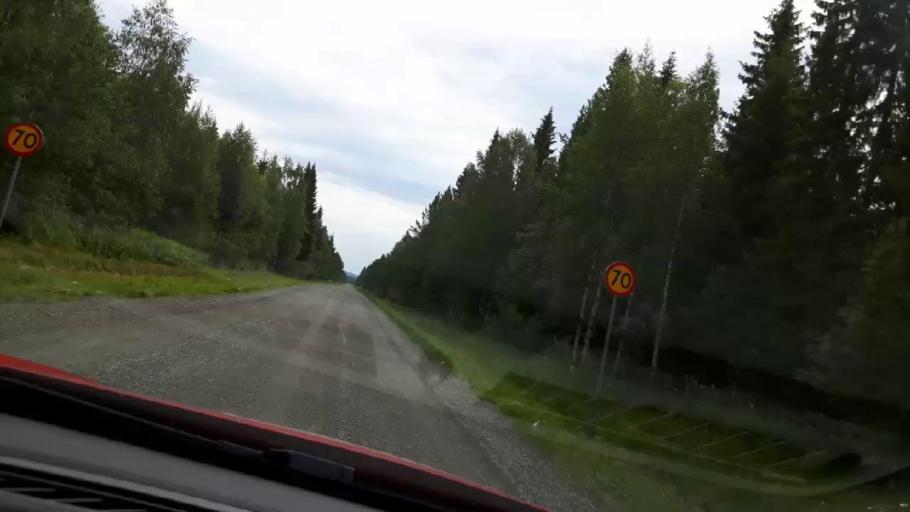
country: SE
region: Jaemtland
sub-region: Stroemsunds Kommun
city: Stroemsund
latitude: 63.7169
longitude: 15.4703
